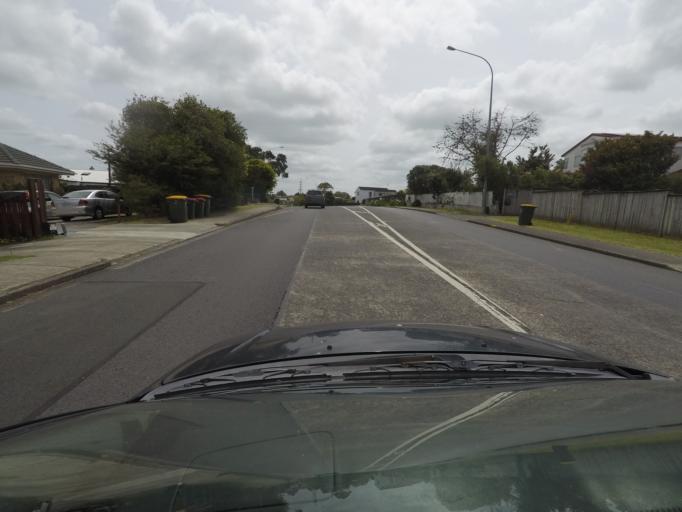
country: NZ
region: Auckland
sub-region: Auckland
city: Pakuranga
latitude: -36.8973
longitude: 174.9211
